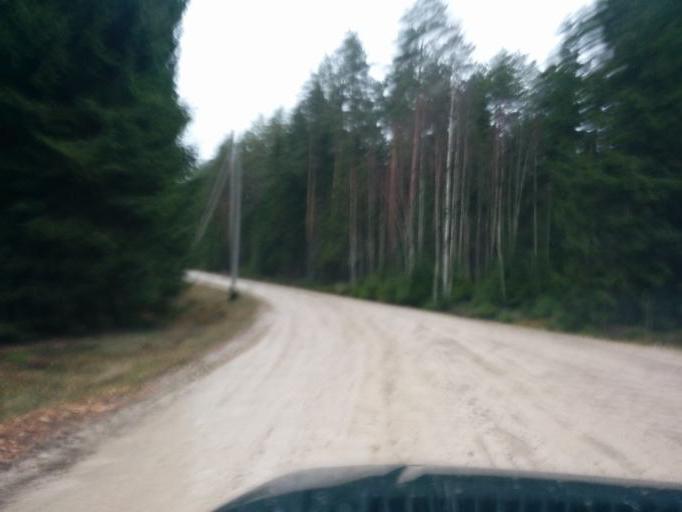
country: LV
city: Tireli
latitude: 56.8235
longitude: 23.7007
